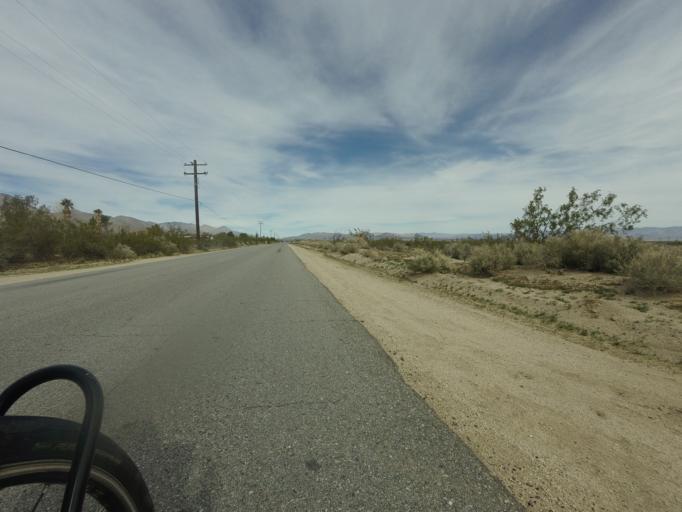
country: US
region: California
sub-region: Kern County
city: Inyokern
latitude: 35.7485
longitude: -117.8425
